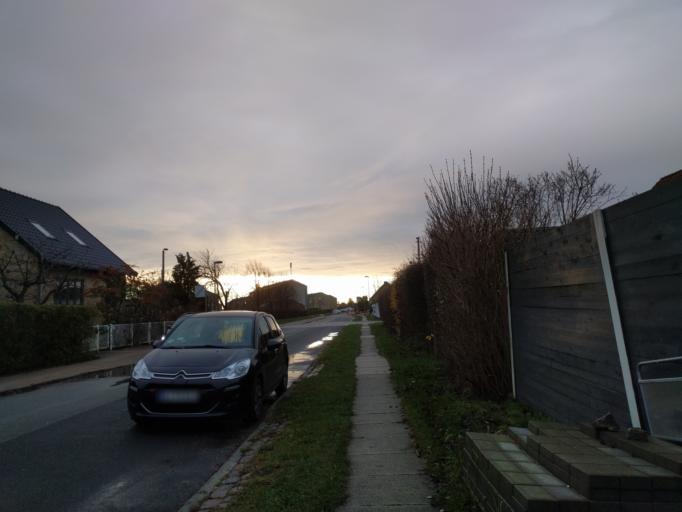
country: DK
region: Capital Region
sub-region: Tarnby Kommune
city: Tarnby
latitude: 55.6487
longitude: 12.6319
